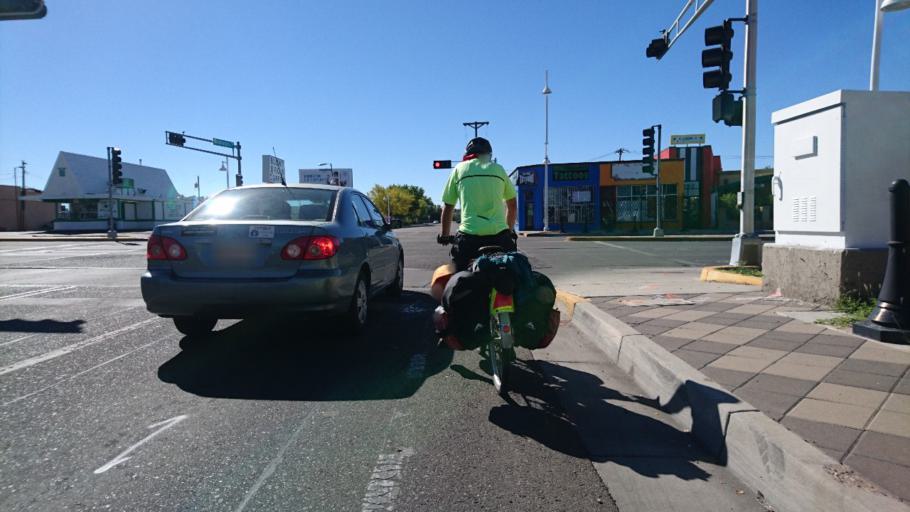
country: US
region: New Mexico
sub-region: Bernalillo County
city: Albuquerque
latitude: 35.0790
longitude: -106.5954
